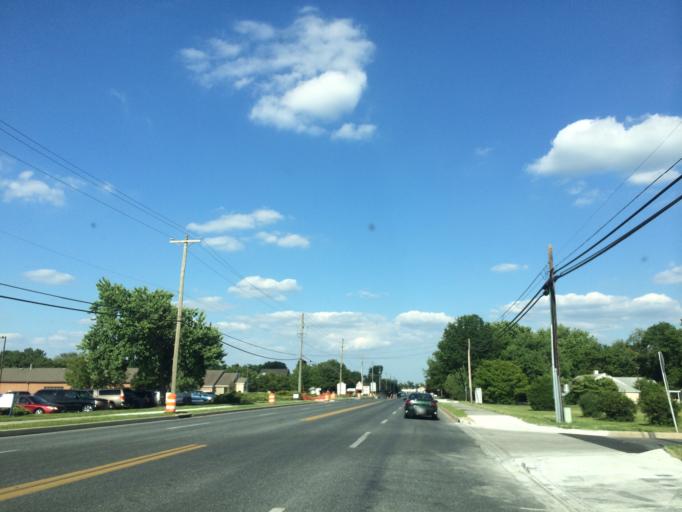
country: US
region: Maryland
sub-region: Wicomico County
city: Salisbury
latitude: 38.3678
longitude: -75.5801
